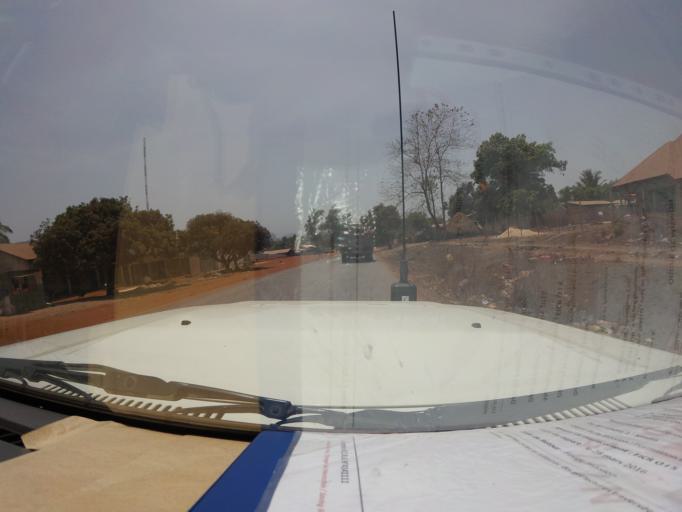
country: GN
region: Kindia
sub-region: Coyah
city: Coyah
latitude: 9.8023
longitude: -13.2843
